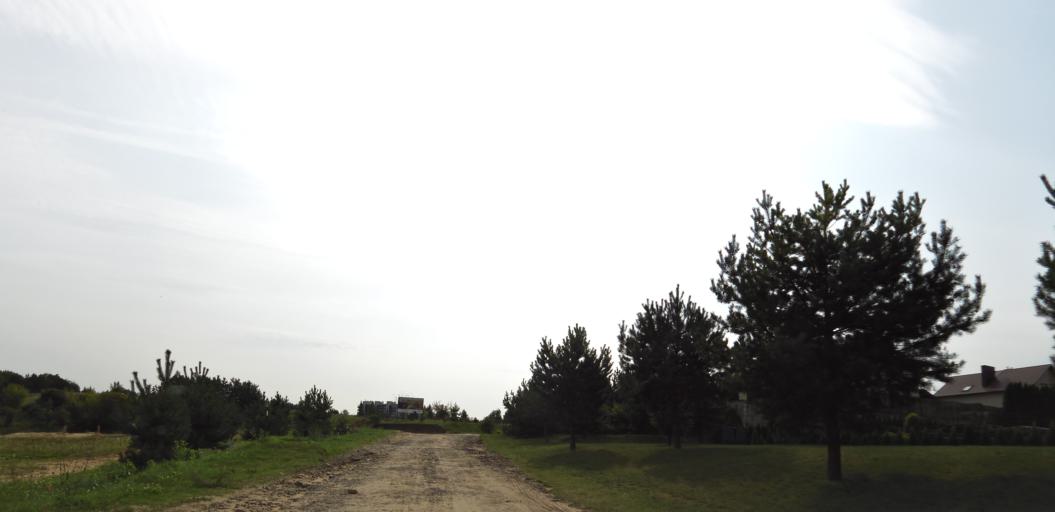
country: LT
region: Vilnius County
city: Pasilaiciai
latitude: 54.7466
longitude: 25.2308
